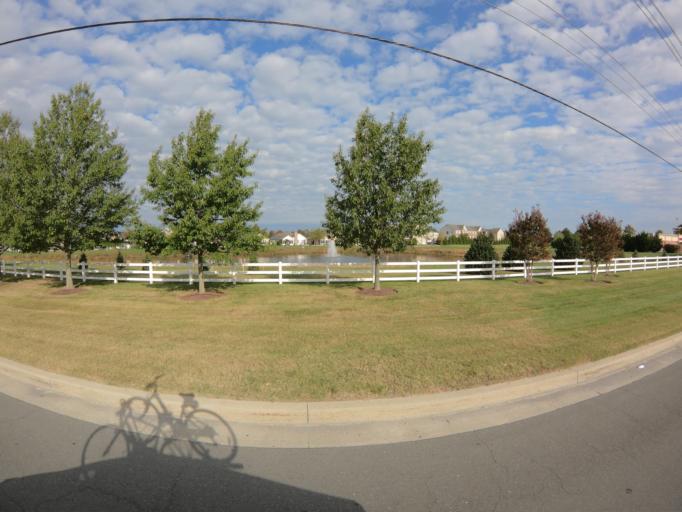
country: US
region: Delaware
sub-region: Sussex County
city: Lewes
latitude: 38.7502
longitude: -75.1692
